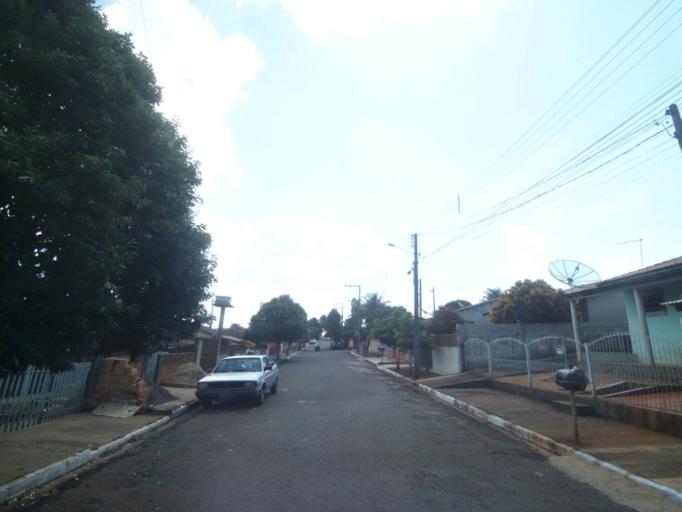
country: BR
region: Parana
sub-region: Sertanopolis
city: Sertanopolis
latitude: -23.0445
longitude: -50.8213
